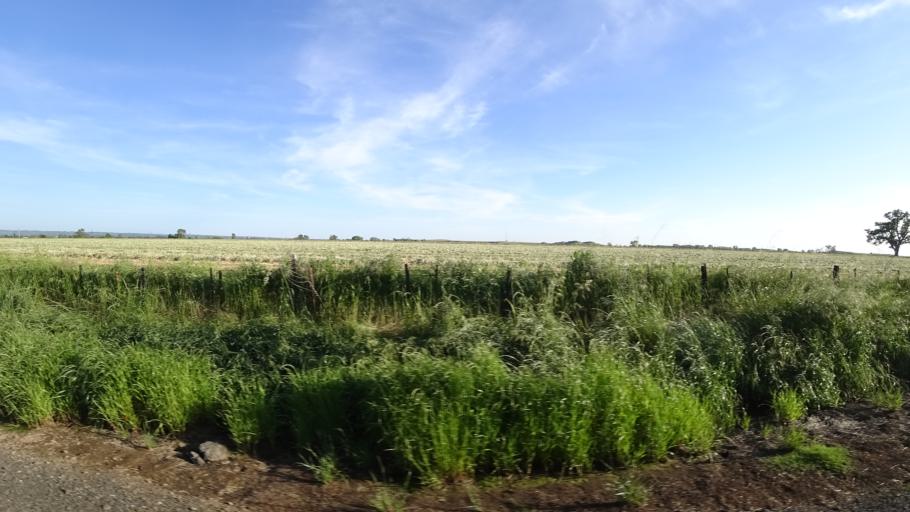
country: US
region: California
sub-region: Placer County
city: Lincoln
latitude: 38.9265
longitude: -121.2983
